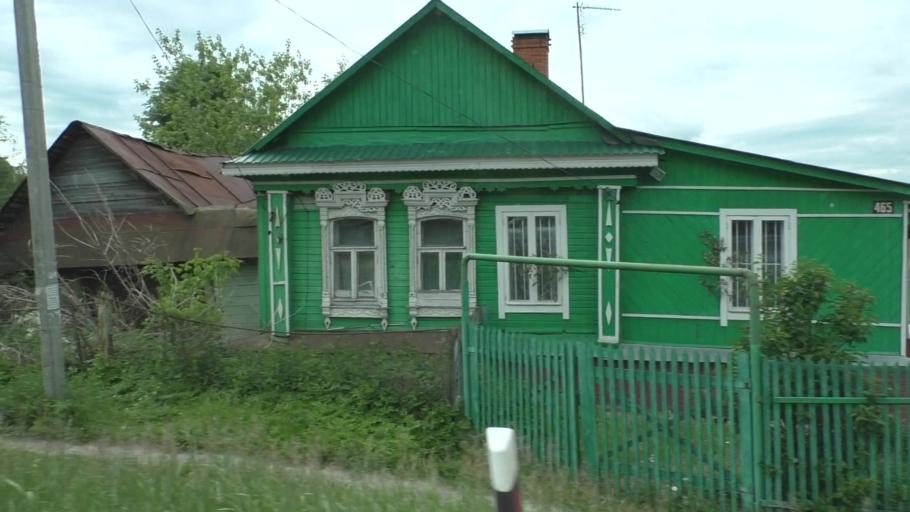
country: RU
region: Moskovskaya
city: Imeni Tsyurupy
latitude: 55.5075
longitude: 38.7656
